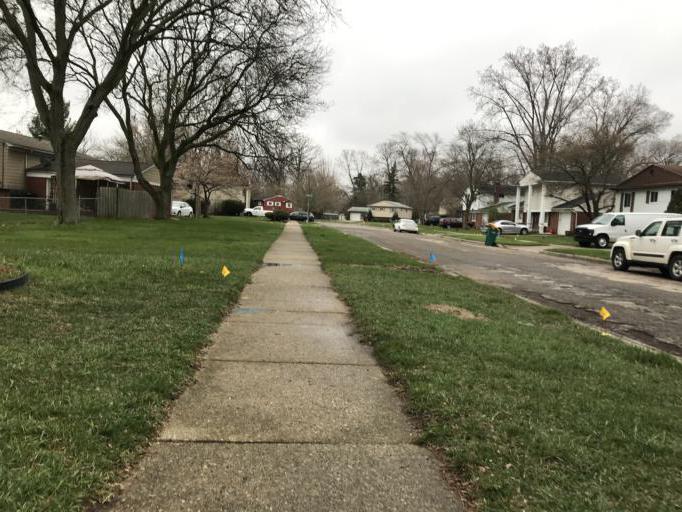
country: US
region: Michigan
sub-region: Oakland County
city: Farmington
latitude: 42.4684
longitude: -83.3441
